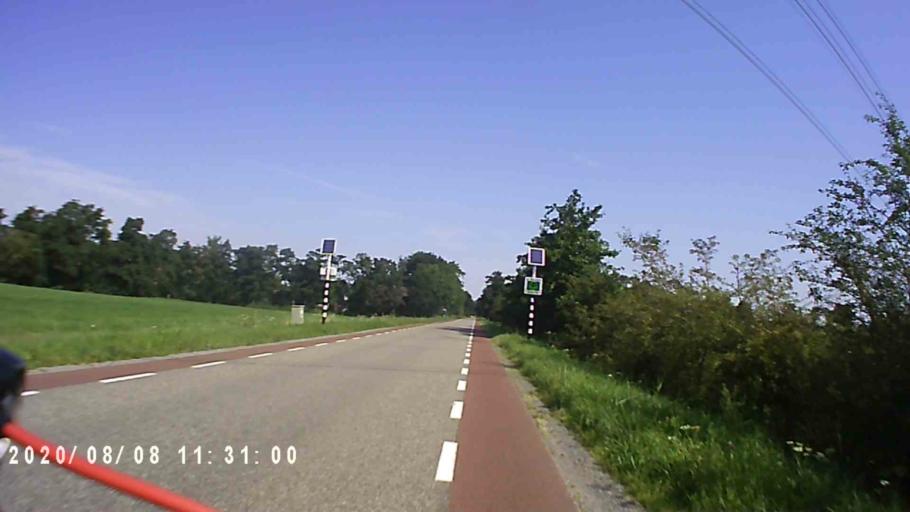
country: NL
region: Groningen
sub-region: Gemeente Leek
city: Leek
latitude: 53.2027
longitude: 6.3876
